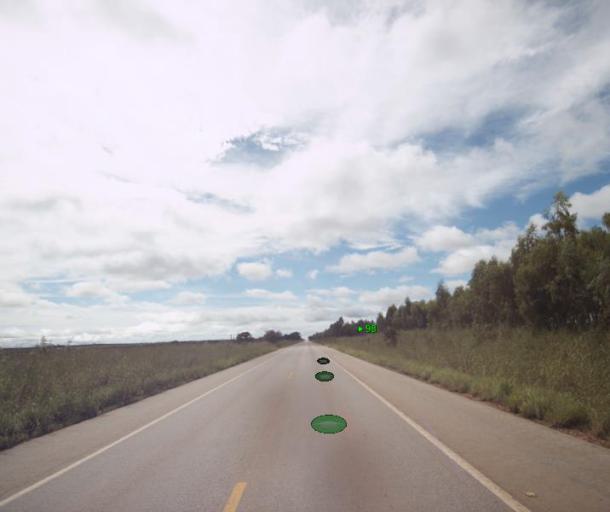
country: BR
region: Goias
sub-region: Barro Alto
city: Barro Alto
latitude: -15.2046
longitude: -48.7337
